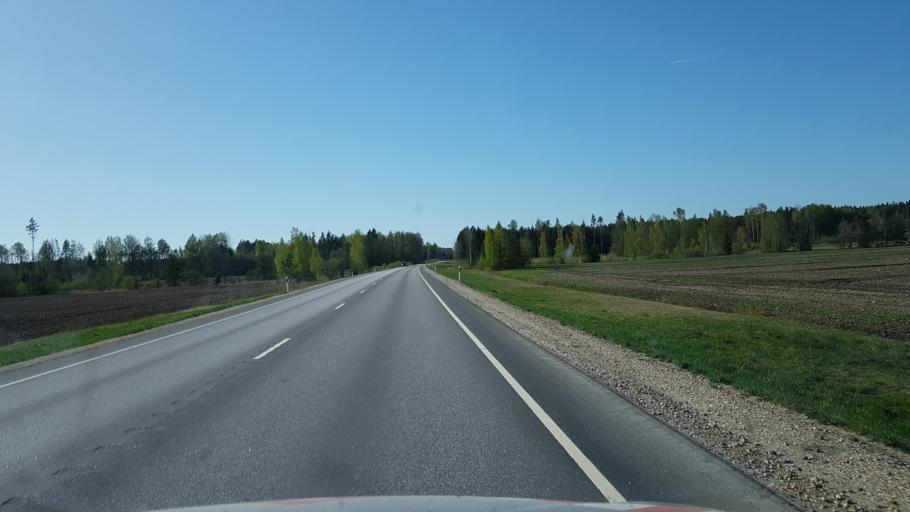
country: EE
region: Paernumaa
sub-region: Paikuse vald
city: Paikuse
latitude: 58.2749
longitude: 24.6260
